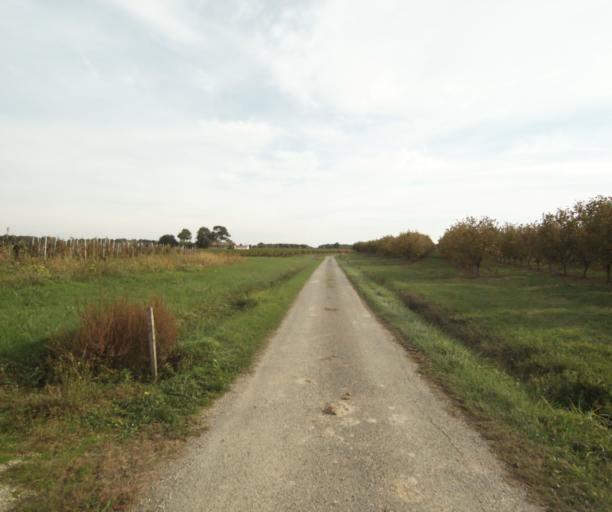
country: FR
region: Midi-Pyrenees
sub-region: Departement du Tarn-et-Garonne
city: Campsas
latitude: 43.9053
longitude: 1.3353
